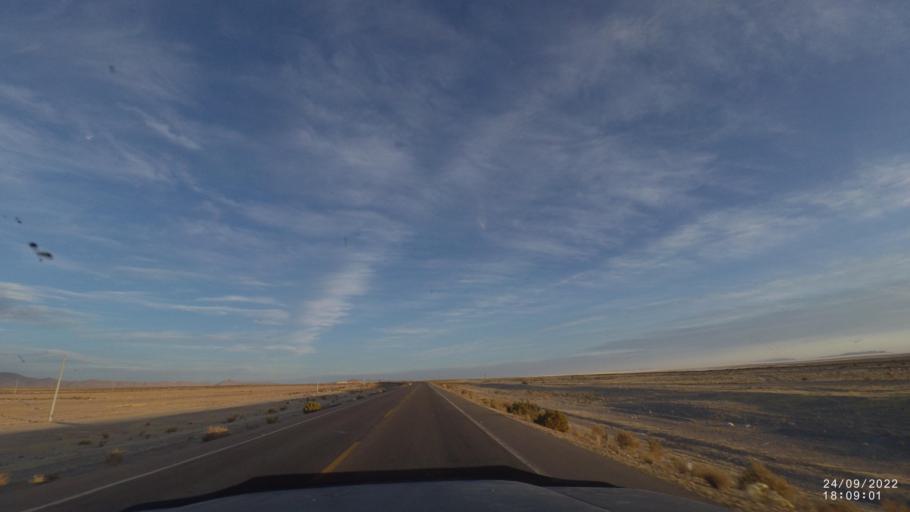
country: BO
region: Potosi
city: Colchani
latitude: -20.3185
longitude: -66.9260
